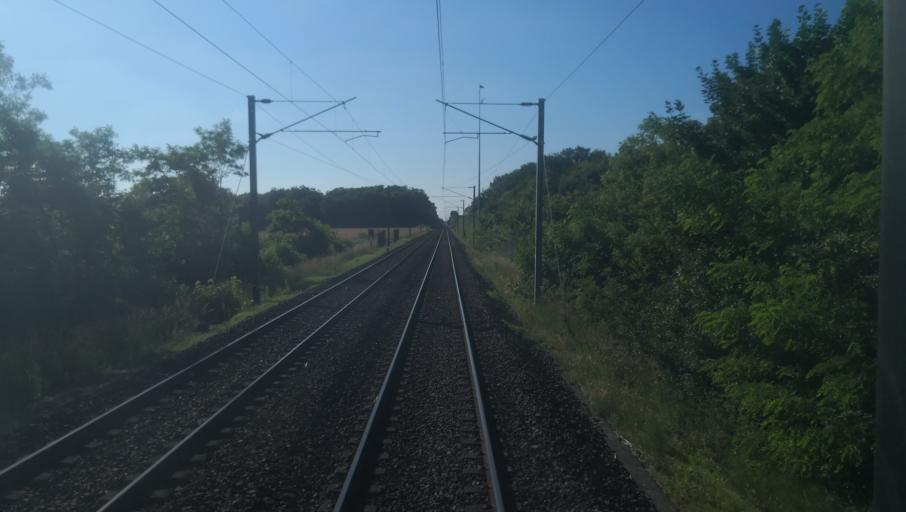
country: FR
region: Centre
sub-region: Departement du Loiret
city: Bonny-sur-Loire
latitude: 47.5763
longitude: 2.8261
